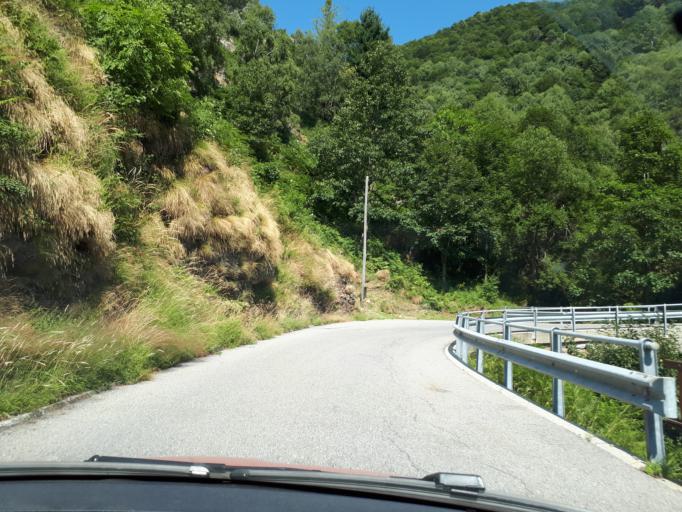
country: CH
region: Ticino
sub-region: Locarno District
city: Magadino
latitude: 46.1052
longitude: 8.8389
